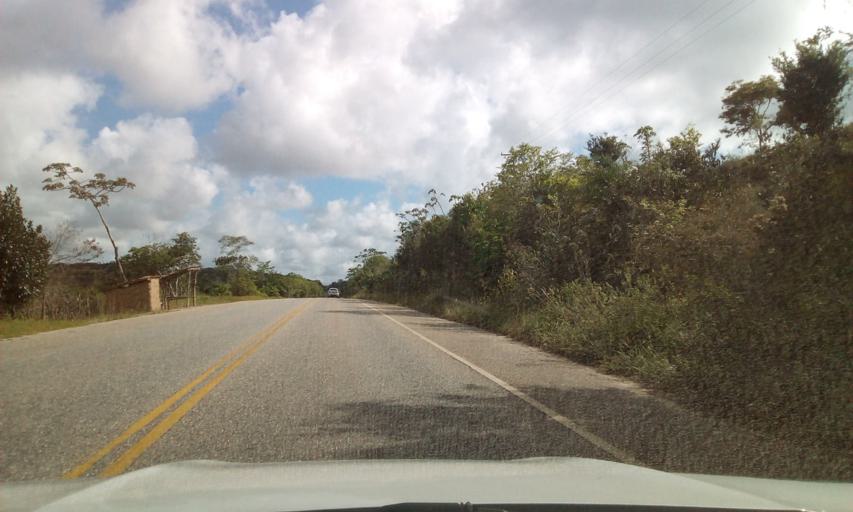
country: BR
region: Sergipe
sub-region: Indiaroba
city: Indiaroba
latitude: -11.4047
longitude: -37.4844
